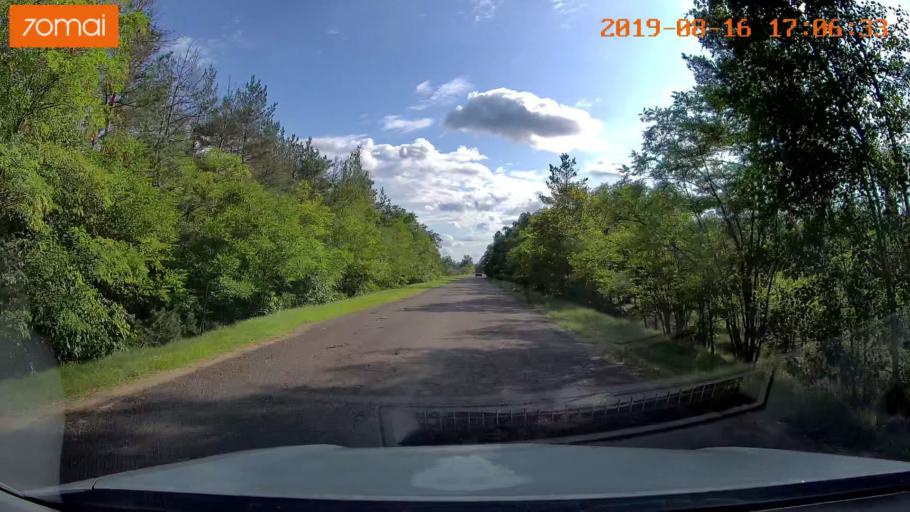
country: BY
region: Mogilev
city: Hlusha
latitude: 53.2256
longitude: 28.9317
